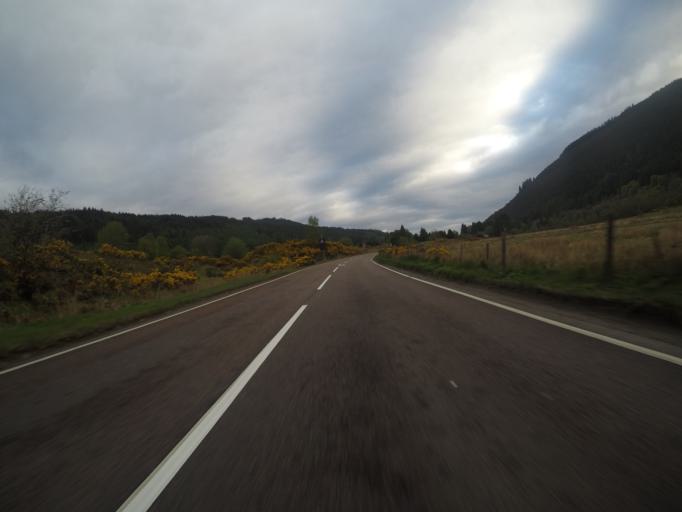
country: GB
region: Scotland
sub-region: Highland
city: Spean Bridge
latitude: 57.0411
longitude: -4.8058
